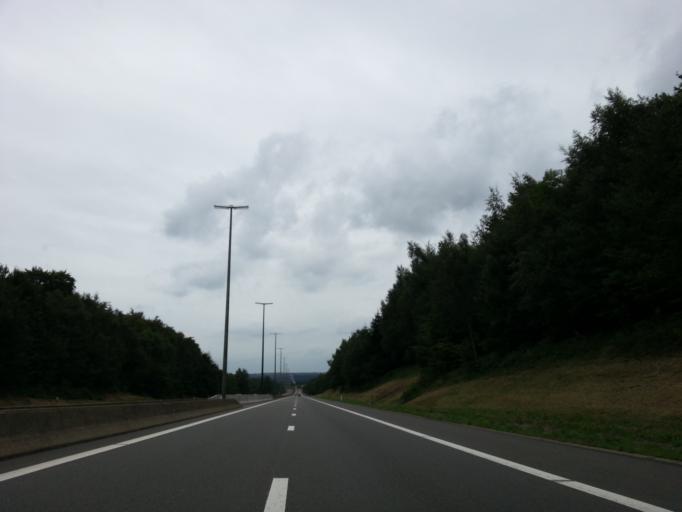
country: BE
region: Wallonia
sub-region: Province de Liege
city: Jalhay
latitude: 50.4997
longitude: 5.9484
